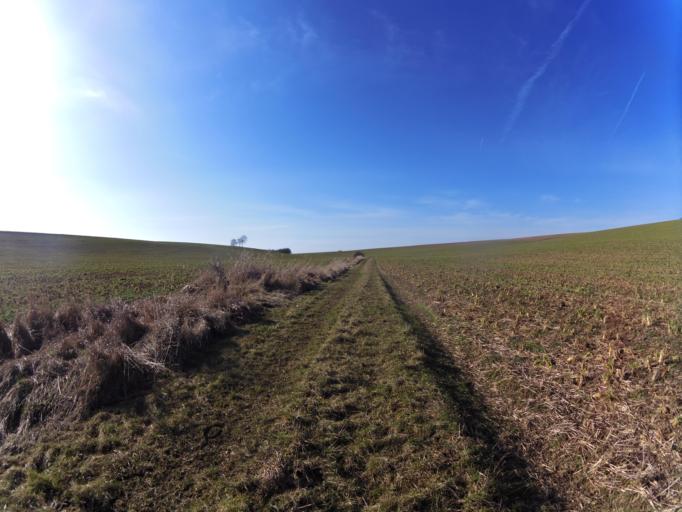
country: DE
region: Bavaria
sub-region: Regierungsbezirk Unterfranken
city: Winterhausen
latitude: 49.6799
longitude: 9.9839
